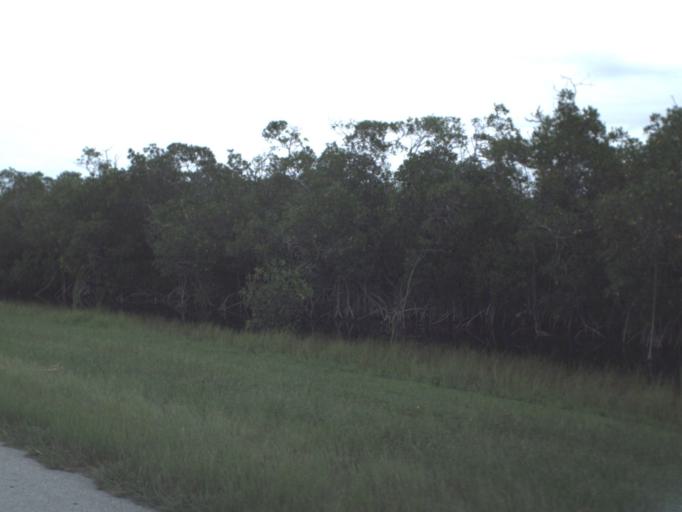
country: US
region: Florida
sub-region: Collier County
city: Marco
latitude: 26.0056
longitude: -81.7016
